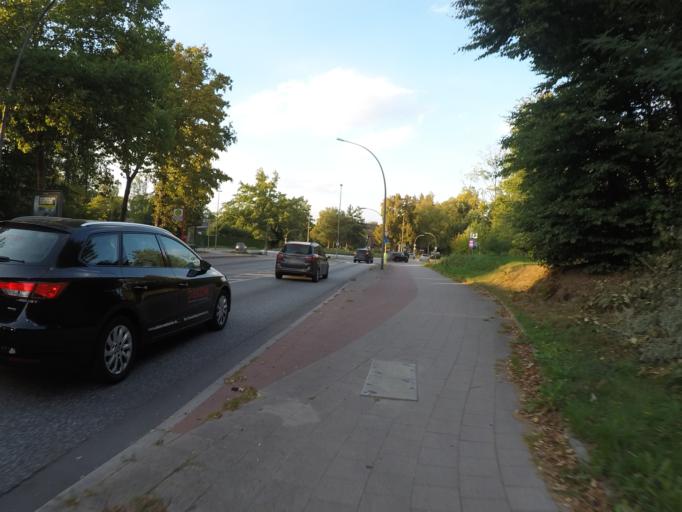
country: DE
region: Hamburg
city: Bergstedt
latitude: 53.6453
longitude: 10.1587
